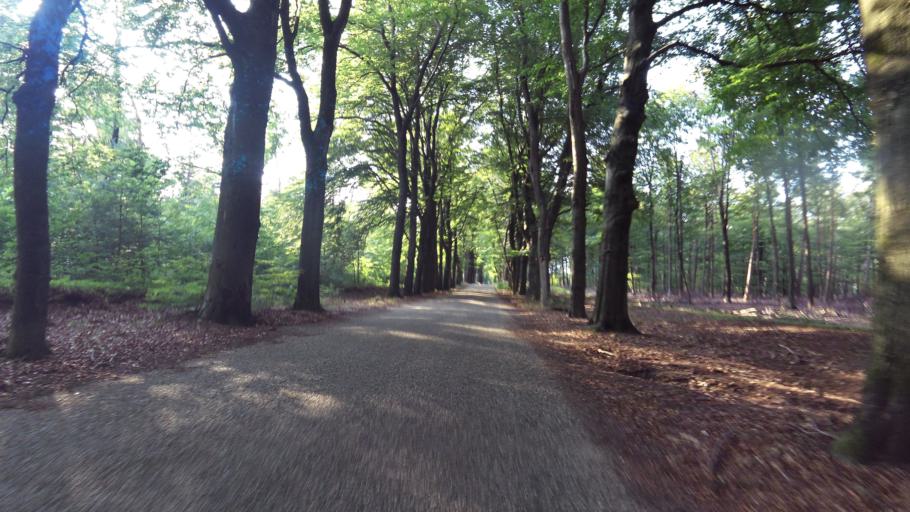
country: NL
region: Gelderland
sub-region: Gemeente Renkum
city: Oosterbeek
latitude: 52.0187
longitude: 5.8455
